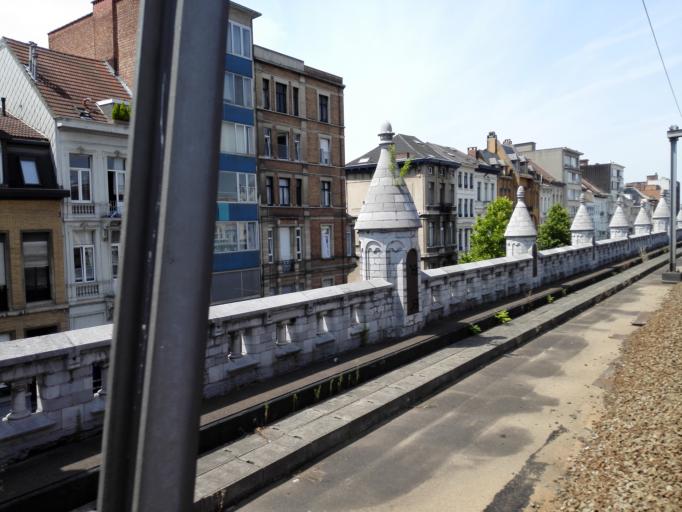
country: BE
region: Flanders
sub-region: Provincie Antwerpen
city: Antwerpen
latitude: 51.2064
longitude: 4.4257
